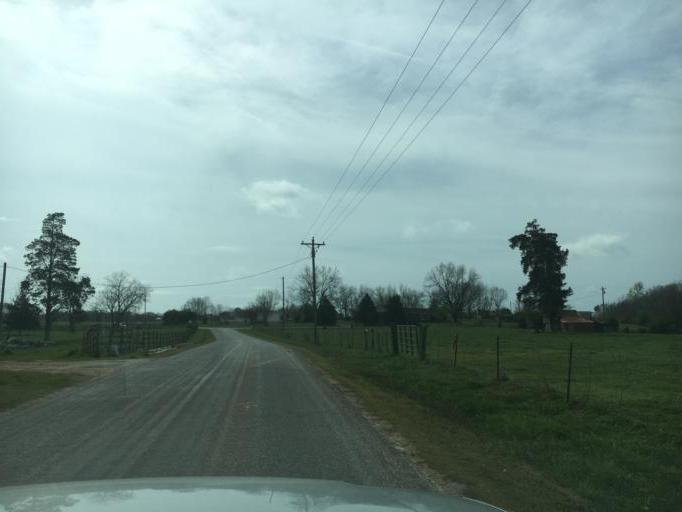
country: US
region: Georgia
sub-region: Franklin County
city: Lavonia
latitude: 34.3639
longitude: -83.0531
